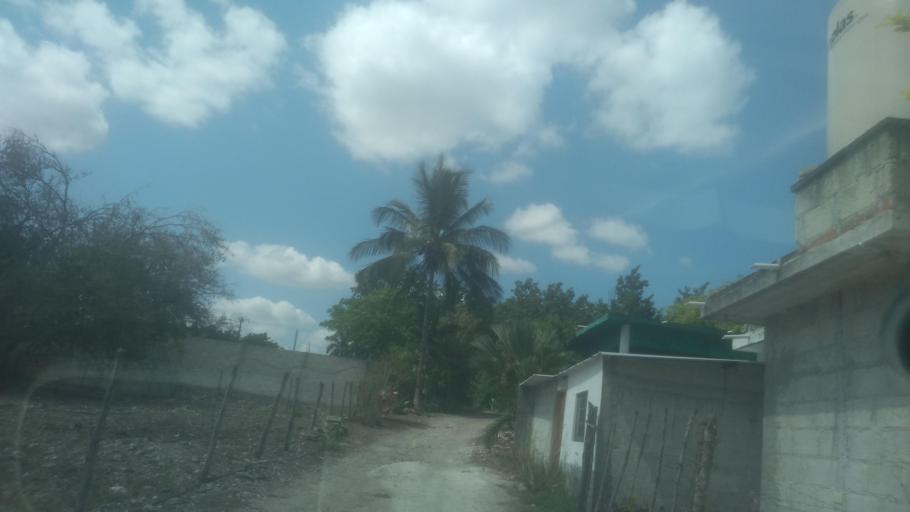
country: MX
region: Veracruz
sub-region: Emiliano Zapata
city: Plan del Rio
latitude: 19.3929
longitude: -96.6333
